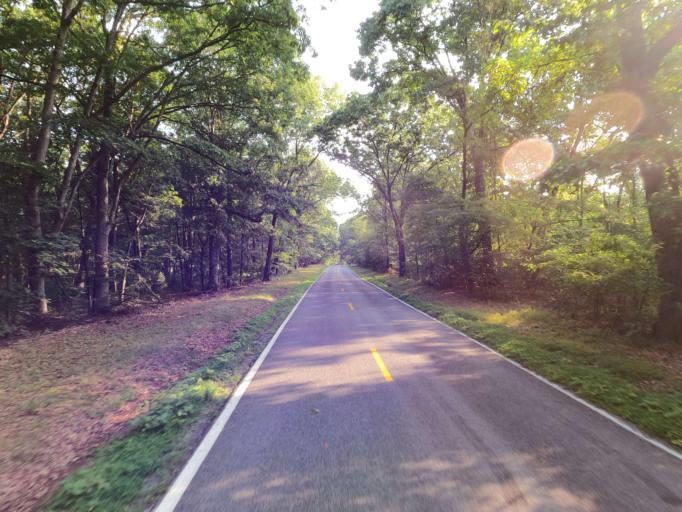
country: US
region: West Virginia
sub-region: Morgan County
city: Berkeley Springs
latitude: 39.6498
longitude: -78.2944
